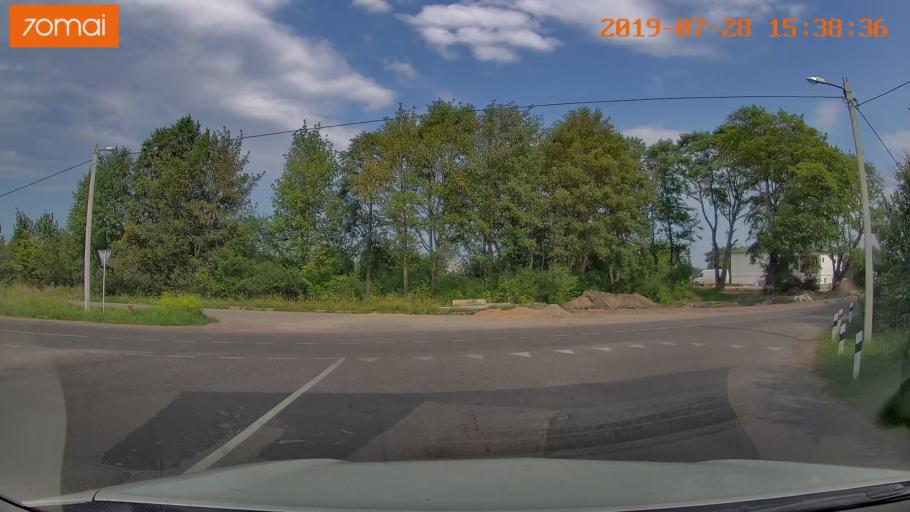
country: RU
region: Kaliningrad
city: Donskoye
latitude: 54.8961
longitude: 20.0185
